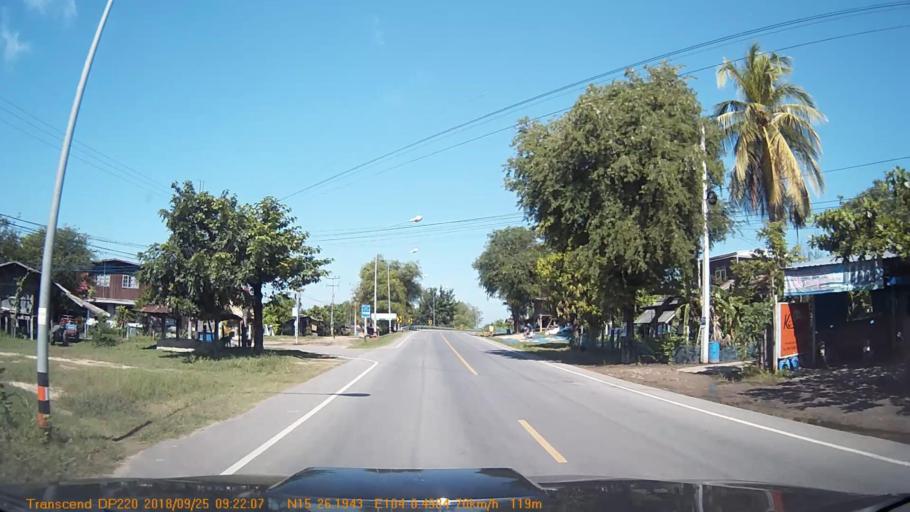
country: TH
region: Roi Et
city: Phon Sai
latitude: 15.4365
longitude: 104.0083
